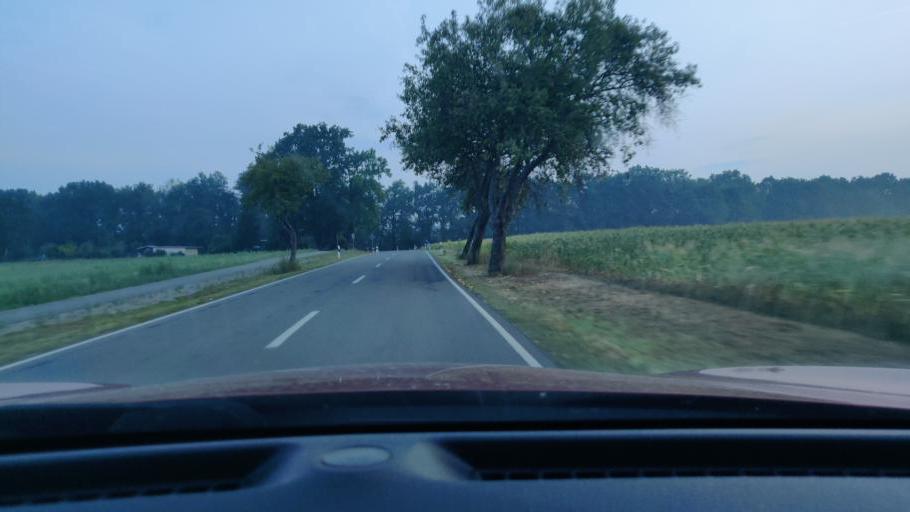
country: DE
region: Saxony
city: Schildau
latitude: 51.5120
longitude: 12.9096
